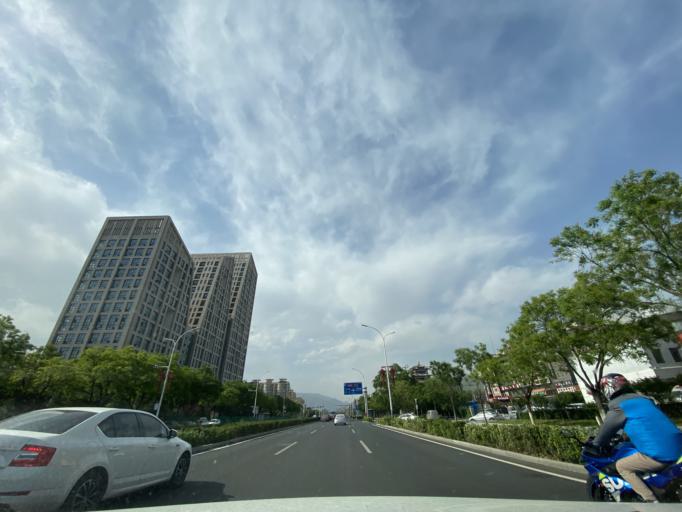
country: CN
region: Beijing
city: Dayu
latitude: 39.9414
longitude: 116.1017
